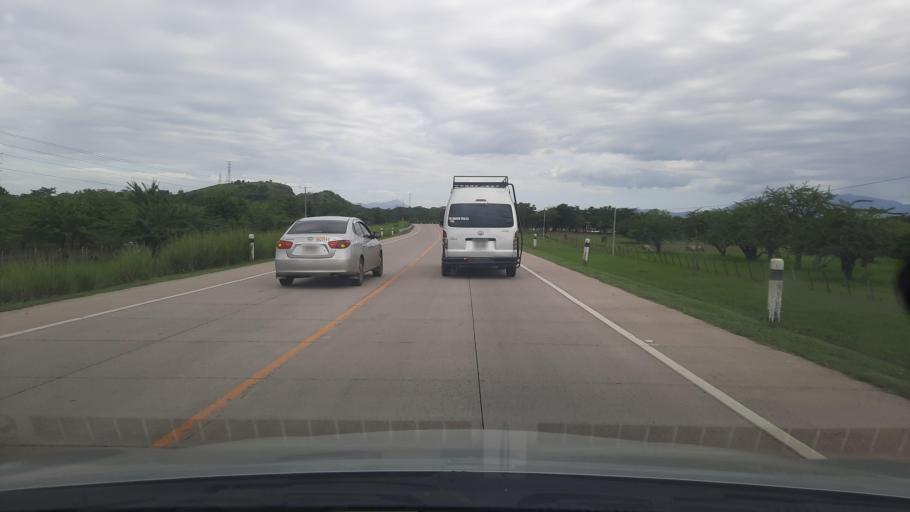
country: NI
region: Chinandega
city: Somotillo
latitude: 12.8766
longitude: -86.8515
